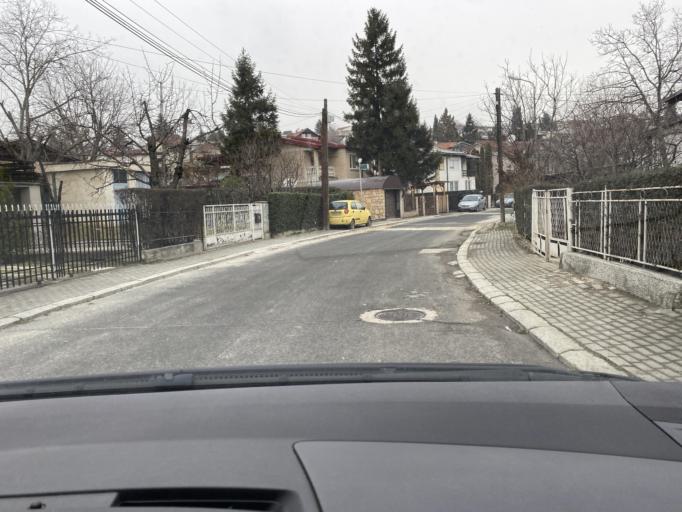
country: MK
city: Radishani
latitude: 42.0581
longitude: 21.4489
